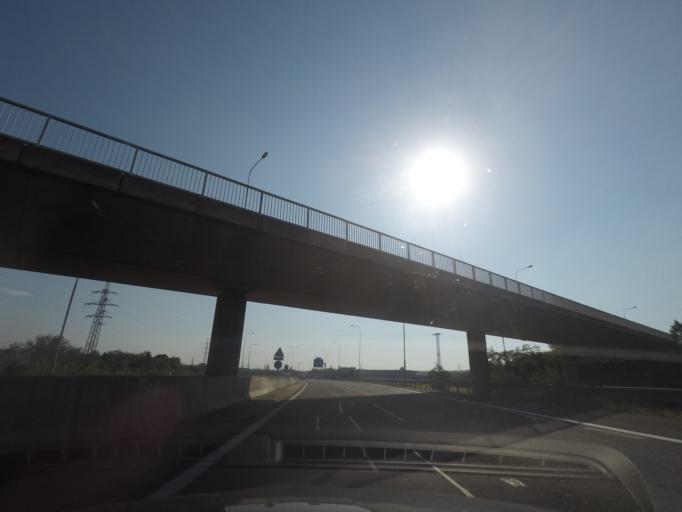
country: CZ
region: Moravskoslezsky
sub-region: Okres Ostrava-Mesto
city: Ostrava
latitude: 49.8611
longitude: 18.2620
